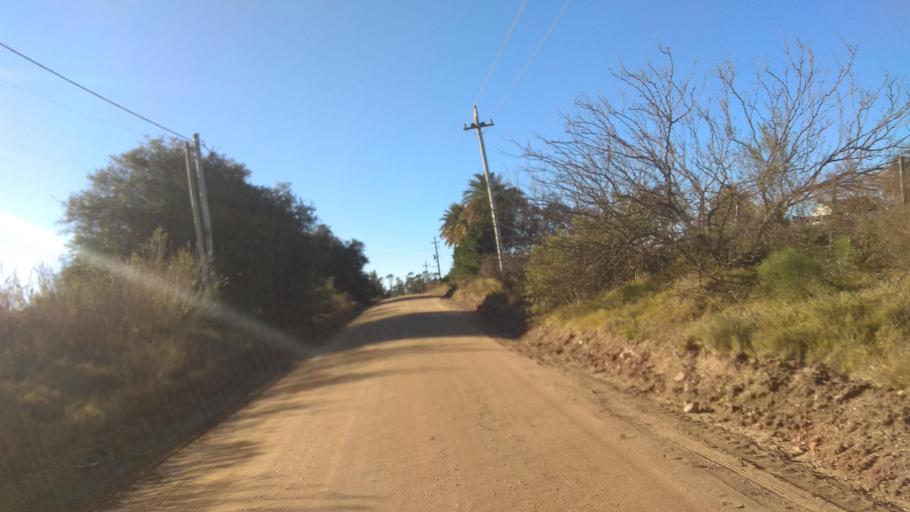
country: UY
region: Florida
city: Florida
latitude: -34.0927
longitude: -56.2482
